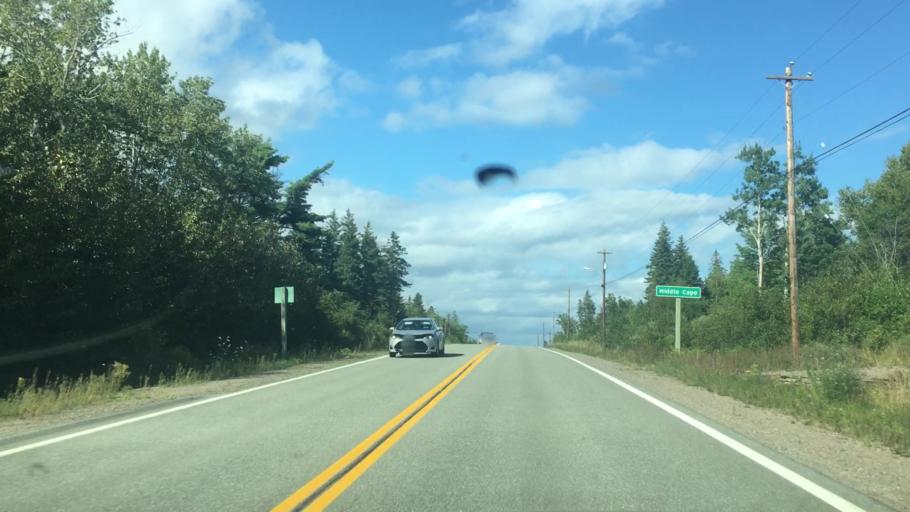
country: CA
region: Nova Scotia
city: Sydney
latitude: 45.8553
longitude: -60.6301
